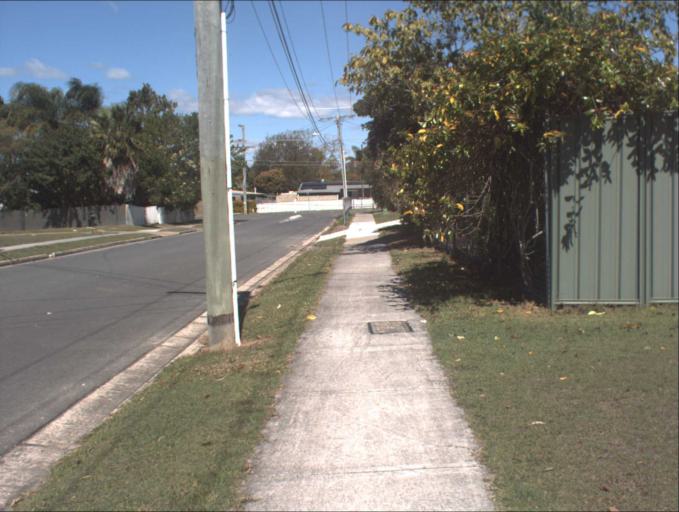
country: AU
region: Queensland
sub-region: Logan
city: Waterford West
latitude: -27.6754
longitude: 153.1030
